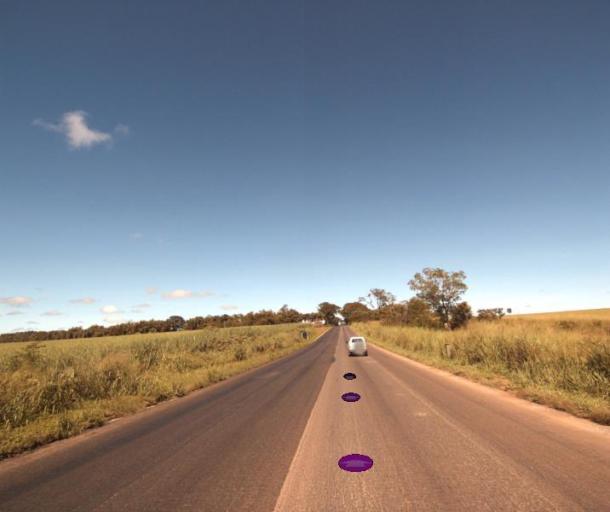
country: BR
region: Goias
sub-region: Itapaci
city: Itapaci
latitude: -15.1281
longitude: -49.5100
